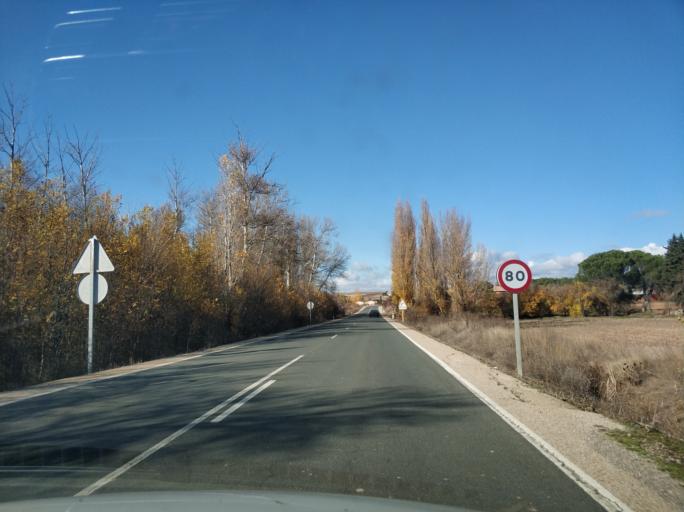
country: ES
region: Castille and Leon
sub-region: Provincia de Soria
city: Almazan
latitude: 41.4723
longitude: -2.5277
